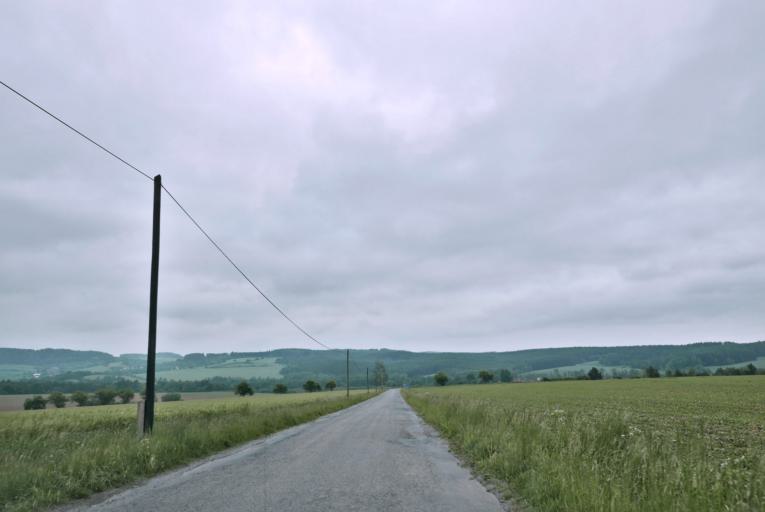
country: CZ
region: Plzensky
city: Zihle
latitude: 49.9914
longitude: 13.3556
